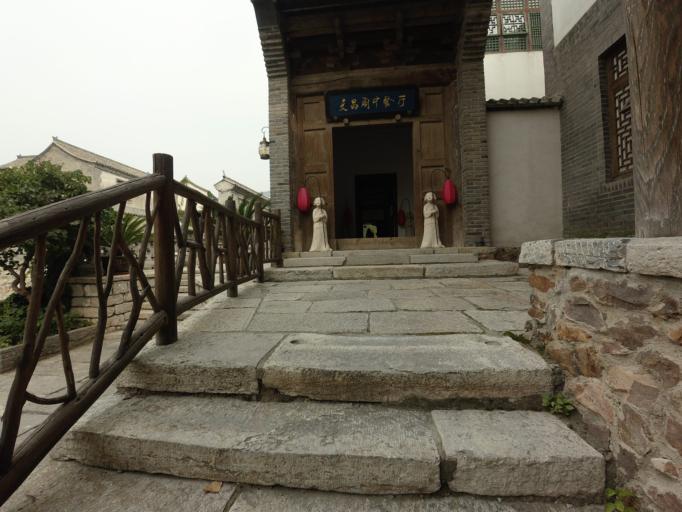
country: CN
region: Beijing
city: Xinchengzi
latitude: 40.6511
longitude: 117.2711
